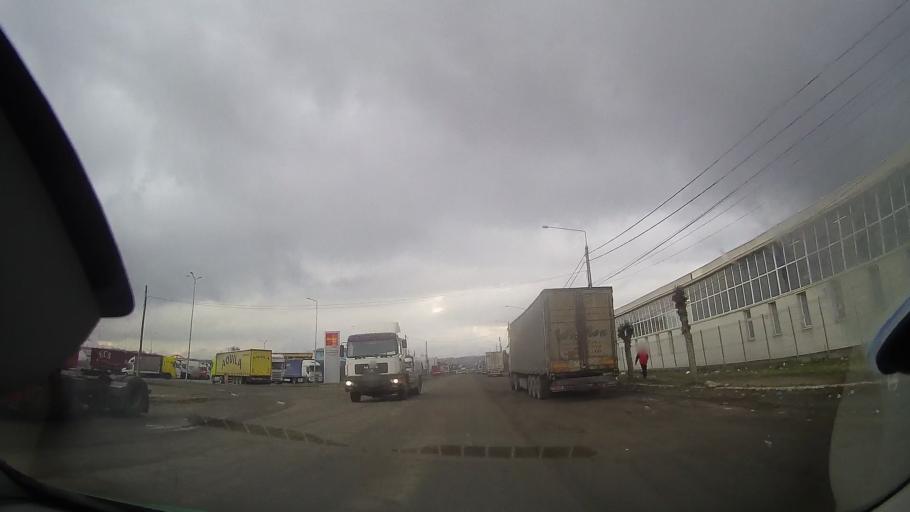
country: RO
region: Cluj
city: Turda
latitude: 46.5507
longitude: 23.7843
